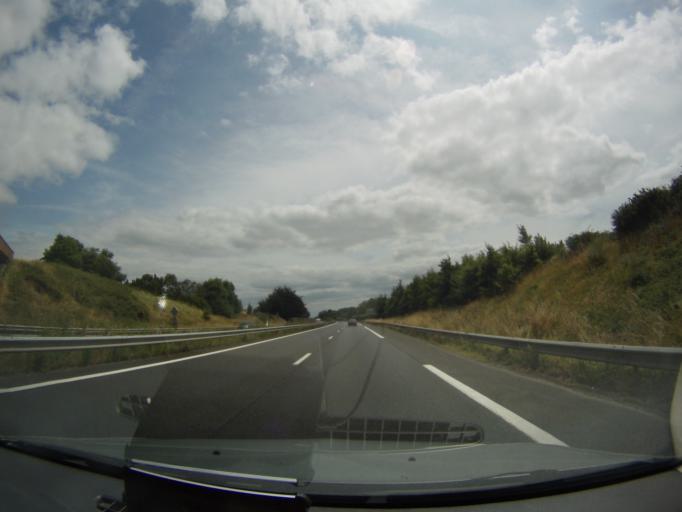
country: FR
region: Pays de la Loire
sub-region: Departement de la Loire-Atlantique
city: Haute-Goulaine
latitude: 47.1805
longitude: -1.4119
